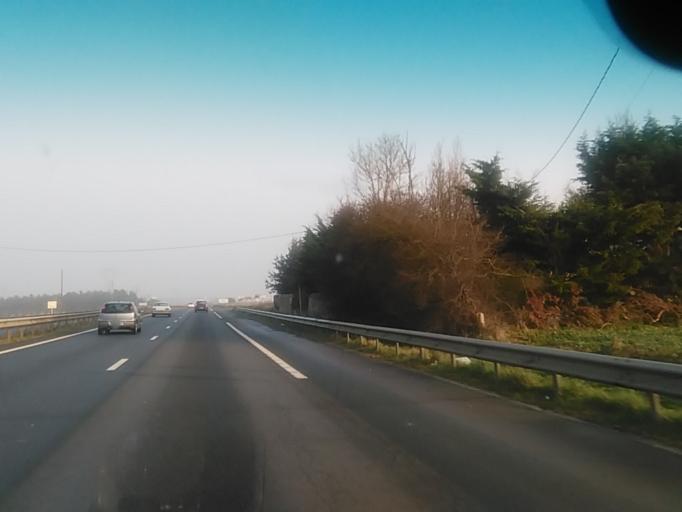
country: FR
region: Lower Normandy
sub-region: Departement du Calvados
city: Ifs
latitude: 49.1278
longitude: -0.3286
